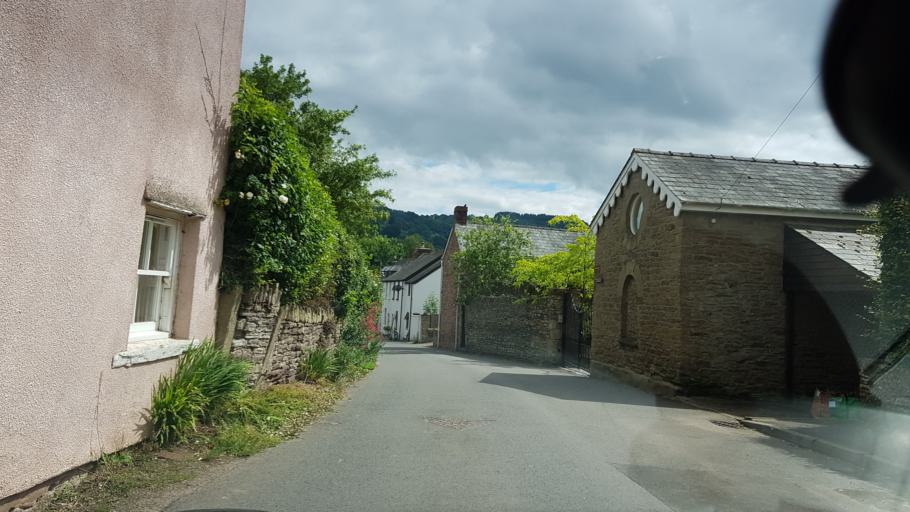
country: GB
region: Wales
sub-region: Monmouthshire
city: Grosmont
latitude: 51.9158
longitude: -2.8682
